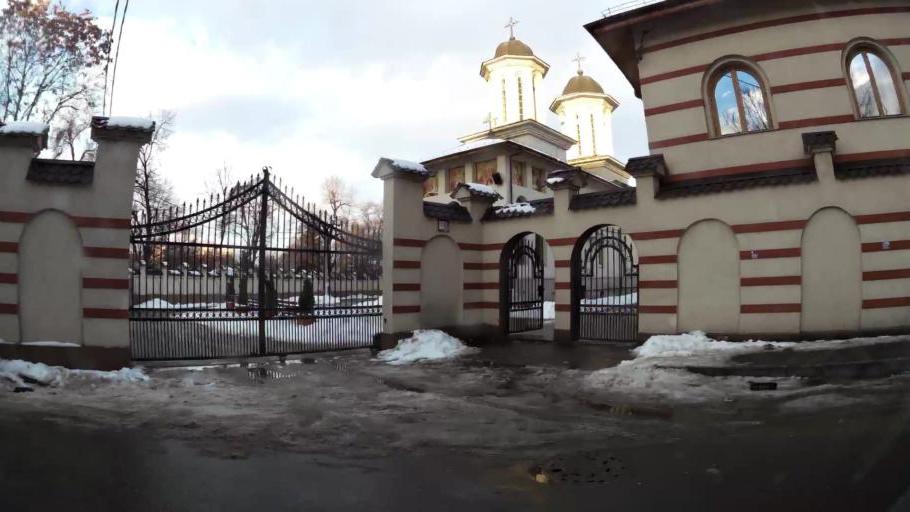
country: RO
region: Ilfov
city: Dobroesti
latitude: 44.4440
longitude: 26.1714
